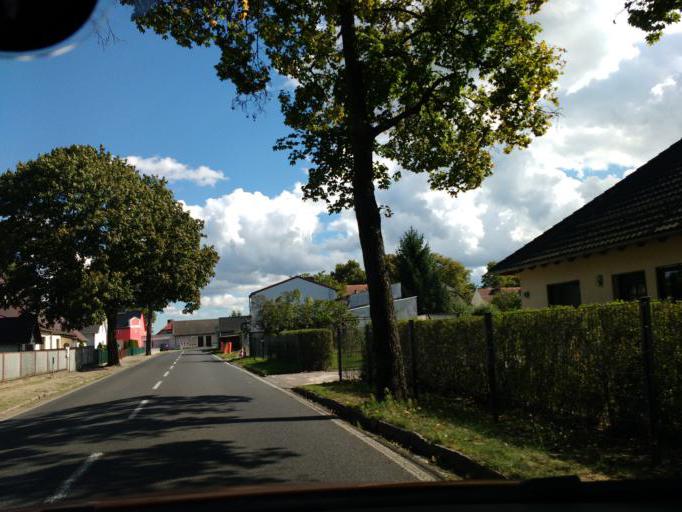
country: DE
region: Brandenburg
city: Bestensee
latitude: 52.2433
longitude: 13.7057
